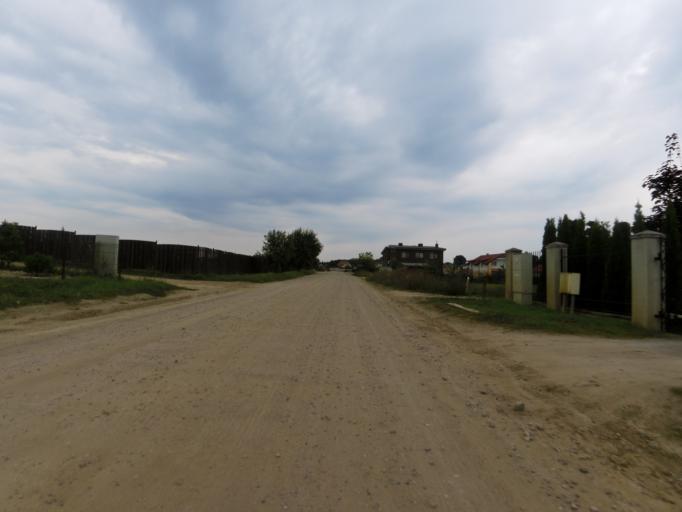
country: LT
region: Vilnius County
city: Pilaite
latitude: 54.7139
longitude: 25.1315
